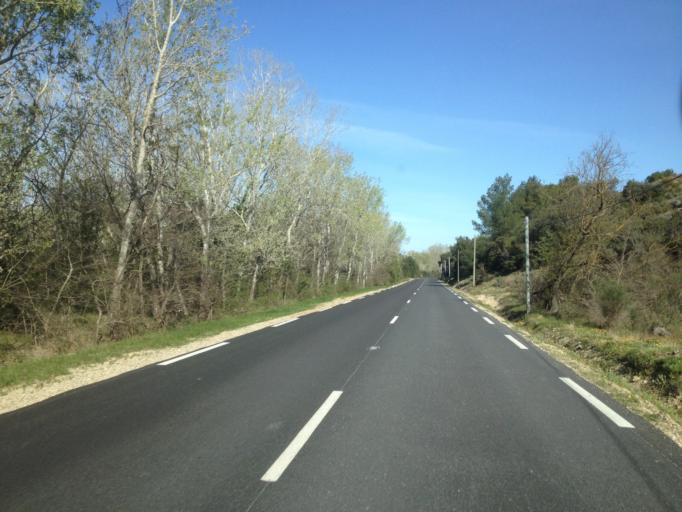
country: FR
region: Languedoc-Roussillon
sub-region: Departement du Gard
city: Roquemaure
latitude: 44.0696
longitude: 4.7880
